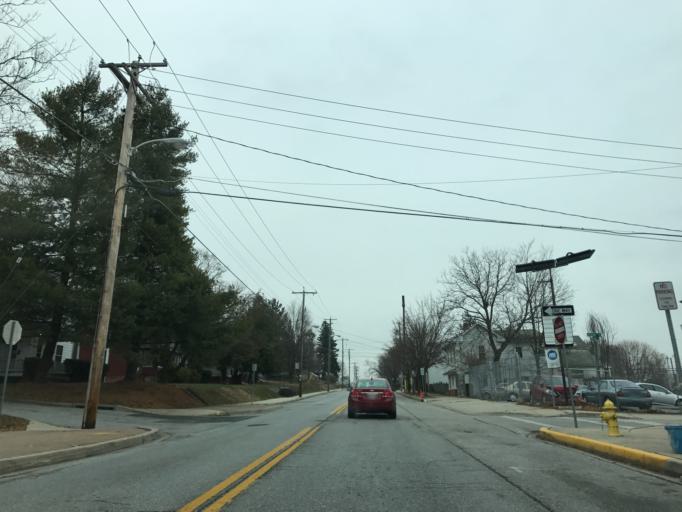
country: US
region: Maryland
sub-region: Carroll County
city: Westminster
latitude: 39.5848
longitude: -76.9991
